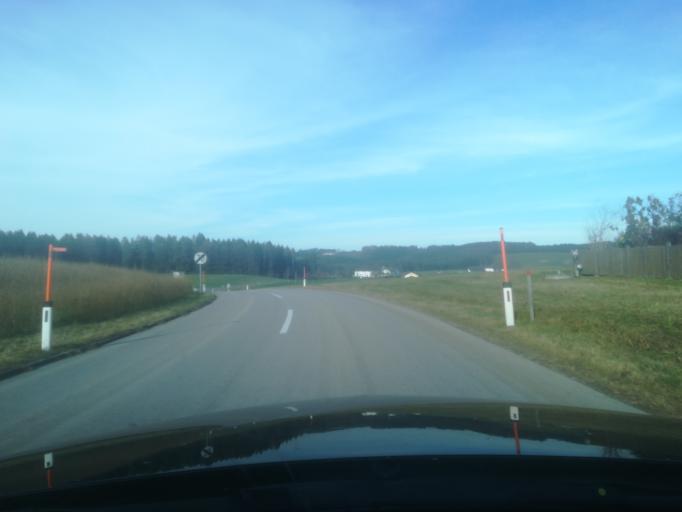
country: AT
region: Upper Austria
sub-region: Politischer Bezirk Perg
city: Perg
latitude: 48.3140
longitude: 14.6632
